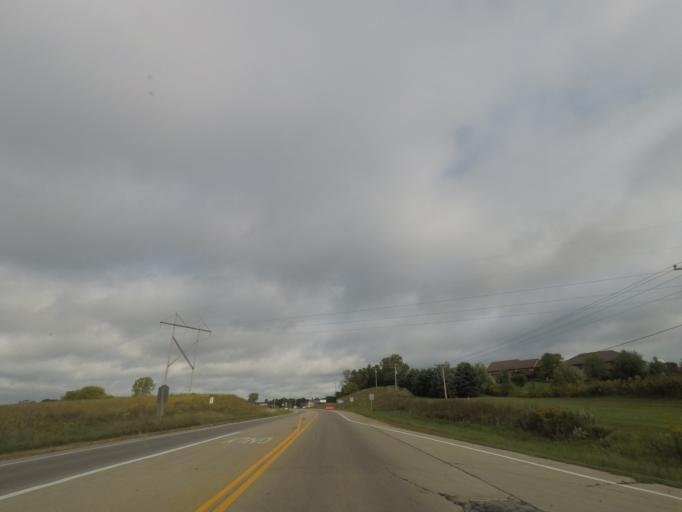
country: US
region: Wisconsin
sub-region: Jefferson County
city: Cambridge
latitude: 43.0102
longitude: -89.0237
